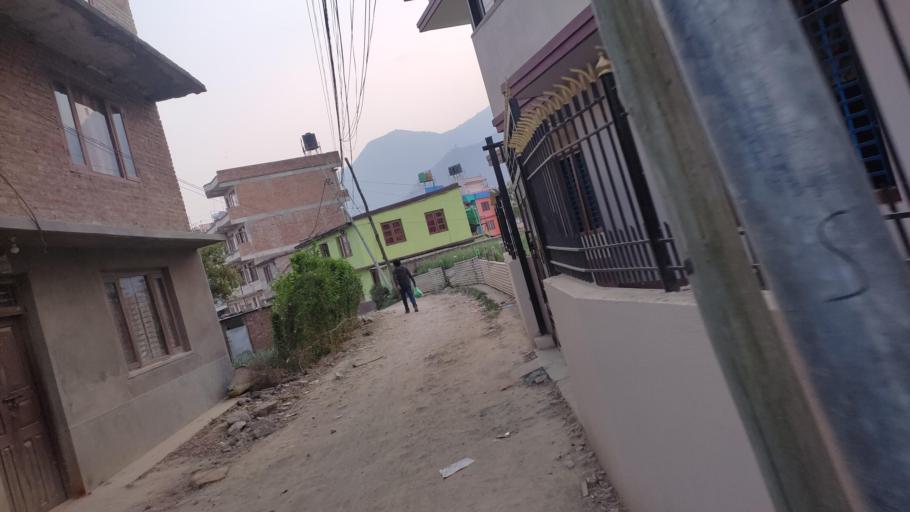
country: NP
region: Central Region
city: Kirtipur
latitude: 27.6668
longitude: 85.2756
